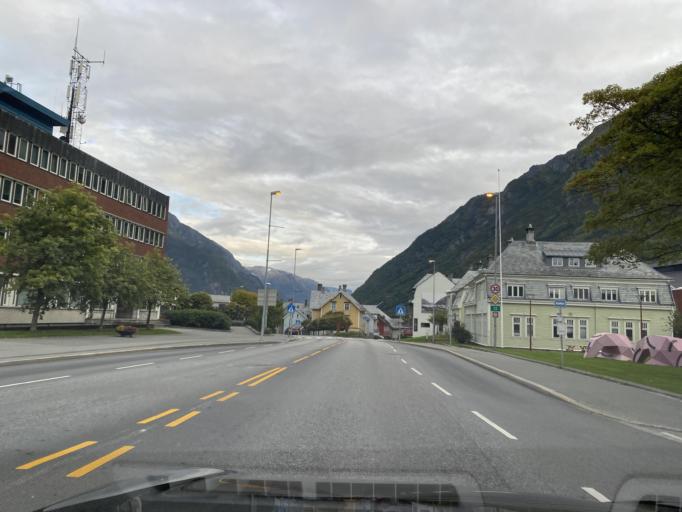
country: NO
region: Hordaland
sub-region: Odda
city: Odda
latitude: 60.0670
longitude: 6.5465
